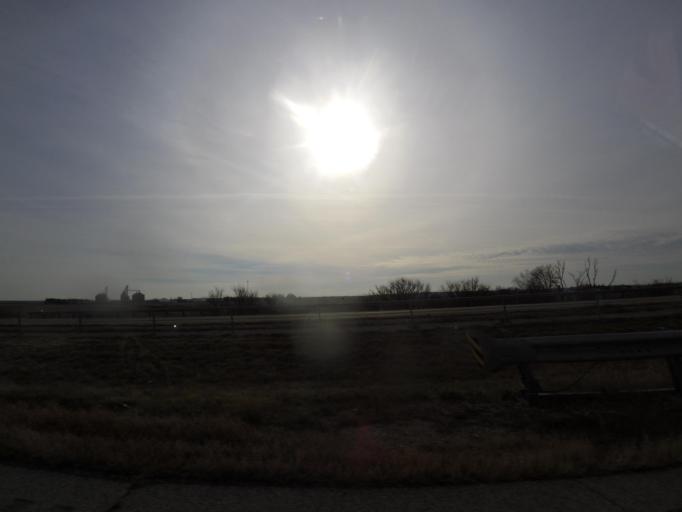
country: US
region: Illinois
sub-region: McLean County
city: Twin Grove
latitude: 40.5406
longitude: -89.0699
